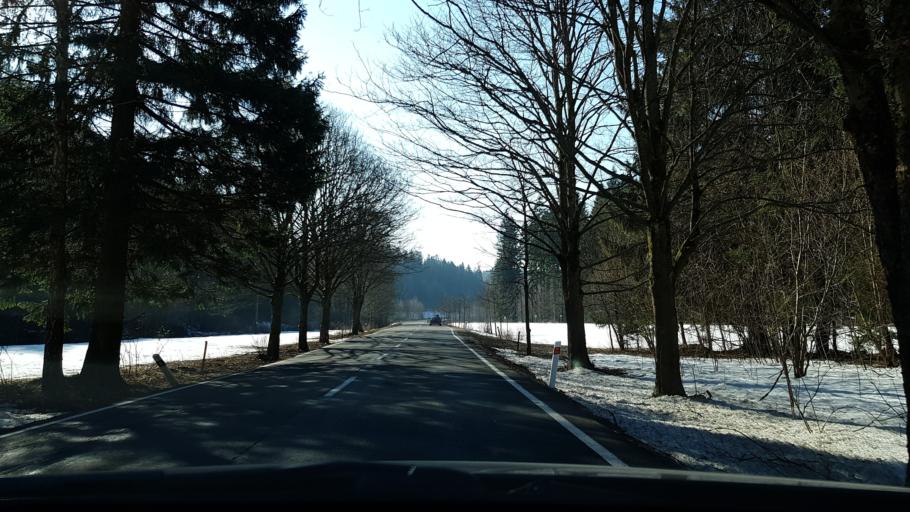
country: CZ
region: Olomoucky
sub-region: Okres Sumperk
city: Stare Mesto
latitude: 50.1230
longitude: 17.0080
